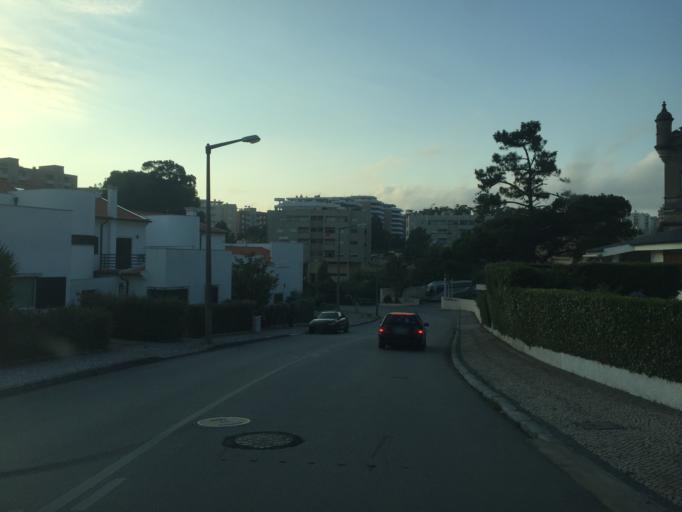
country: PT
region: Coimbra
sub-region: Figueira da Foz
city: Figueira da Foz
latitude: 40.1581
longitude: -8.8645
